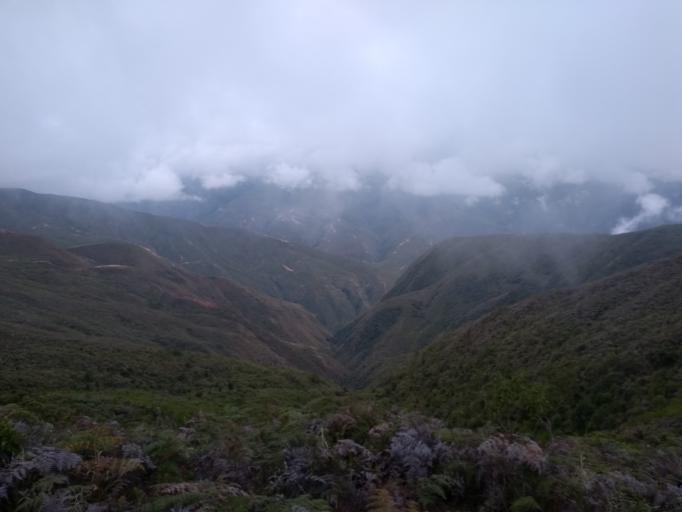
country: CO
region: Cesar
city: Manaure Balcon del Cesar
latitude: 10.1944
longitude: -73.0047
